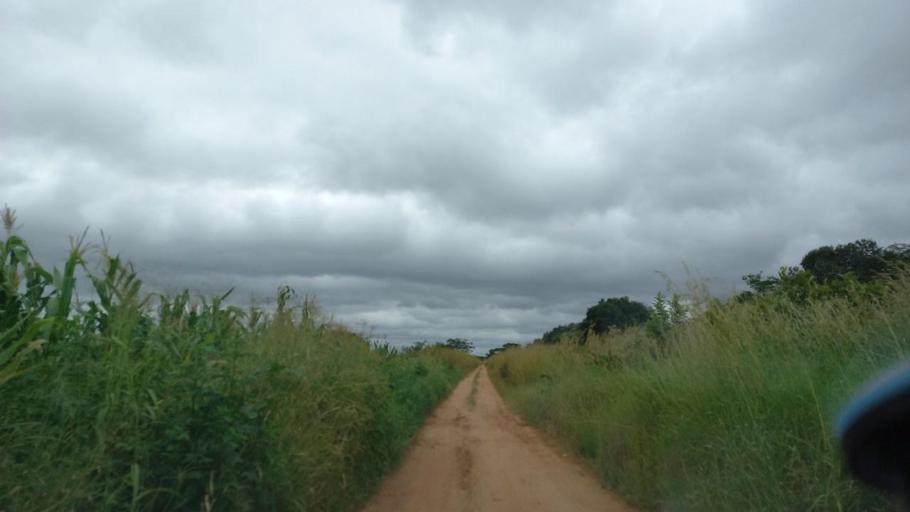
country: ZM
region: Lusaka
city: Lusaka
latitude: -15.1314
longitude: 28.3693
